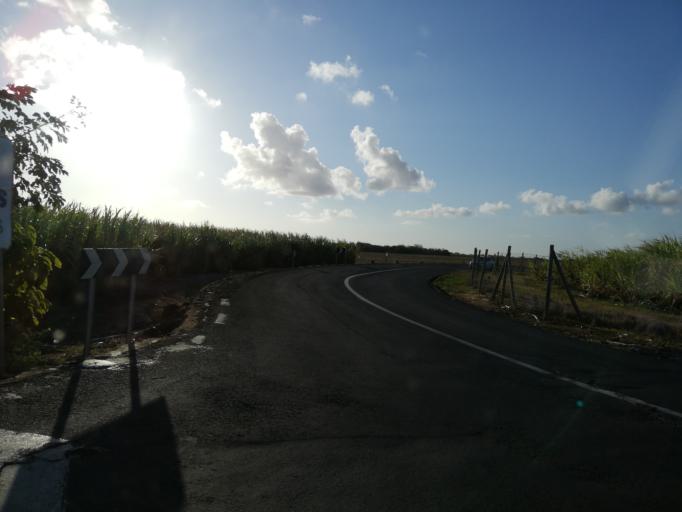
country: MU
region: Pamplemousses
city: Grande Pointe aux Piments
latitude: -20.0817
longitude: 57.5256
